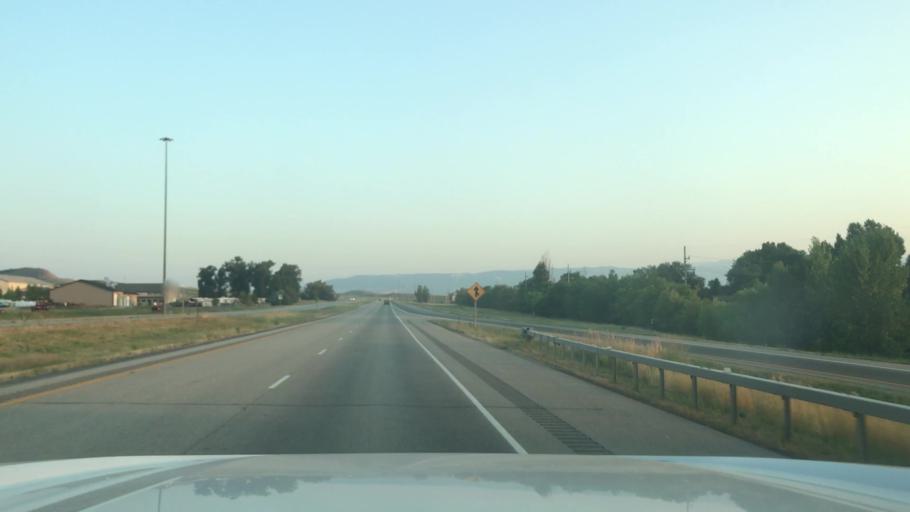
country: US
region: Wyoming
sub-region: Sheridan County
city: Sheridan
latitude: 44.7714
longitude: -106.9369
